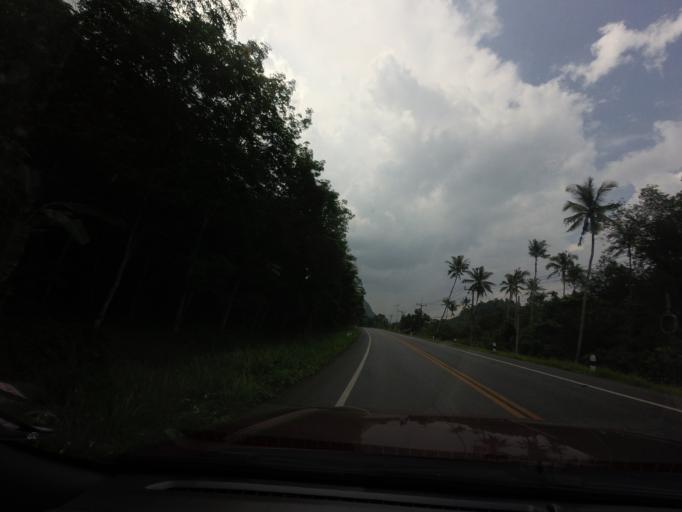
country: TH
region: Yala
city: Ban Nang Sata
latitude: 6.2424
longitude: 101.2198
